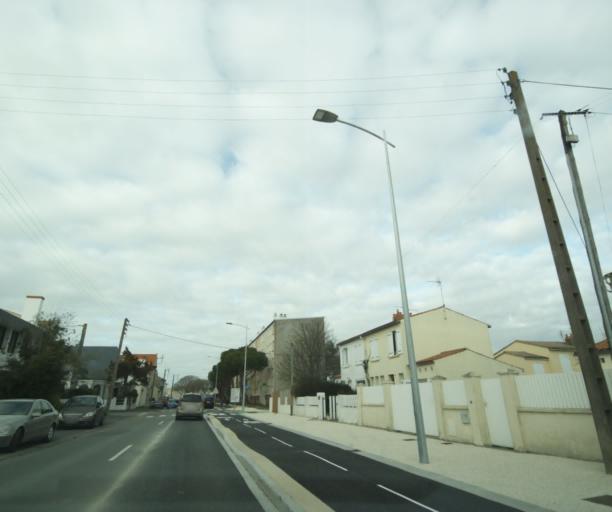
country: FR
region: Poitou-Charentes
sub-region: Departement de la Charente-Maritime
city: La Rochelle
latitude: 46.1682
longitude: -1.1637
